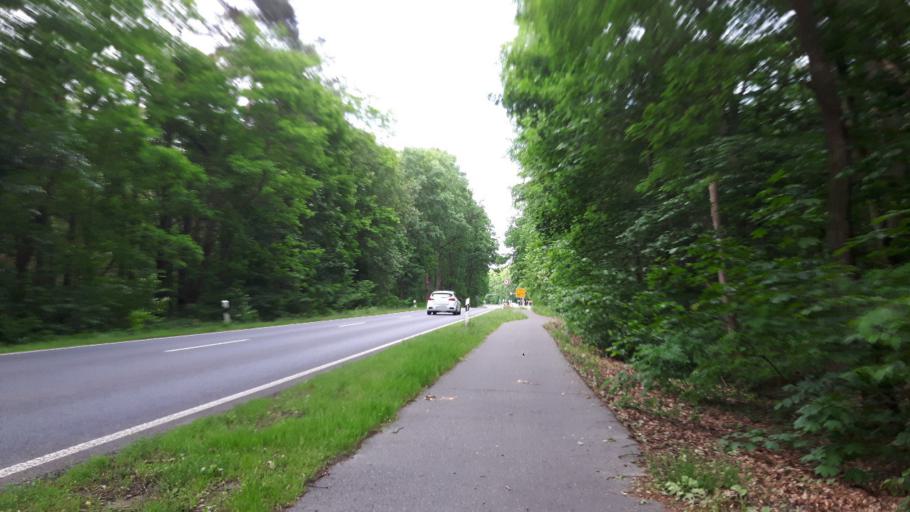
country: DE
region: Brandenburg
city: Michendorf
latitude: 52.3418
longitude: 13.0443
